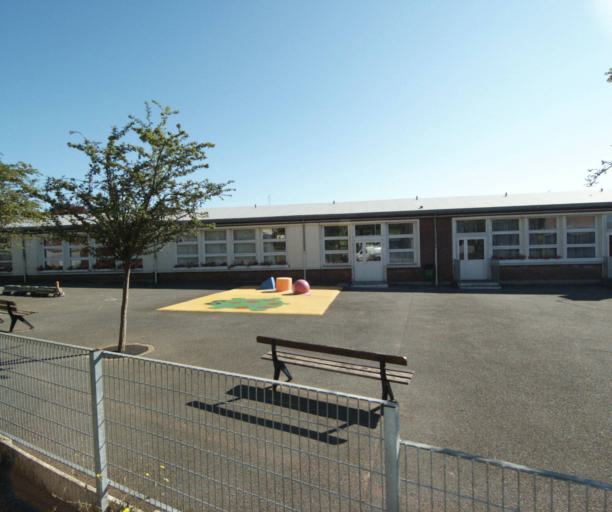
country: FR
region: Nord-Pas-de-Calais
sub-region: Departement du Nord
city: Mouvaux
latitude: 50.7016
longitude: 3.1477
